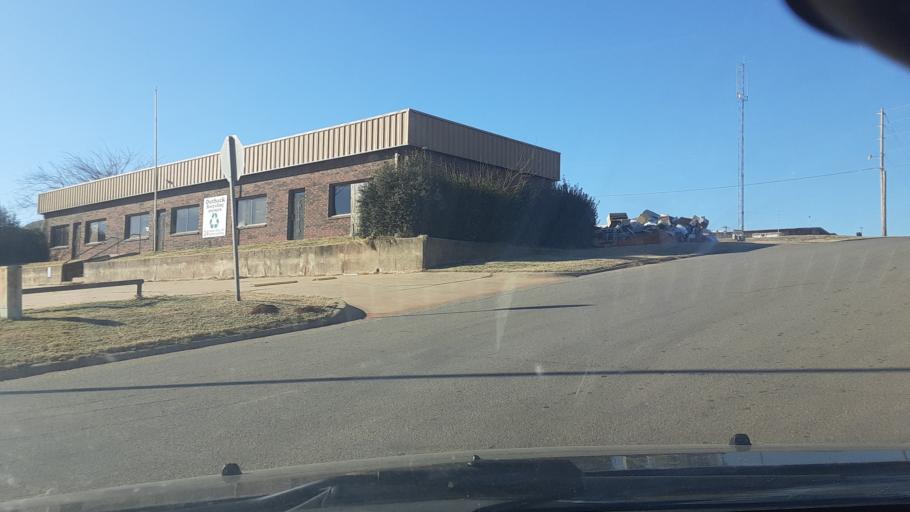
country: US
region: Oklahoma
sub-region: Logan County
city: Guthrie
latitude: 35.8588
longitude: -97.4255
